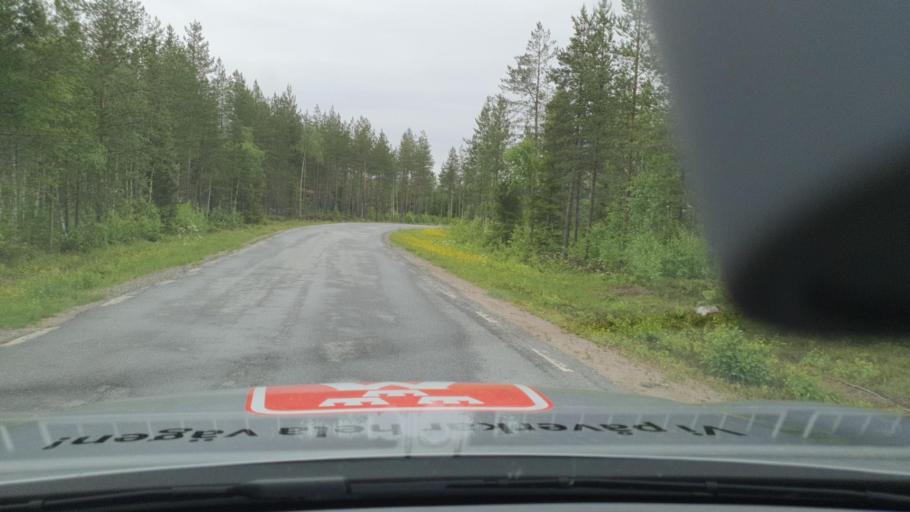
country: SE
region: Norrbotten
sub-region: Lulea Kommun
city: Ranea
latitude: 65.8287
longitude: 22.3187
